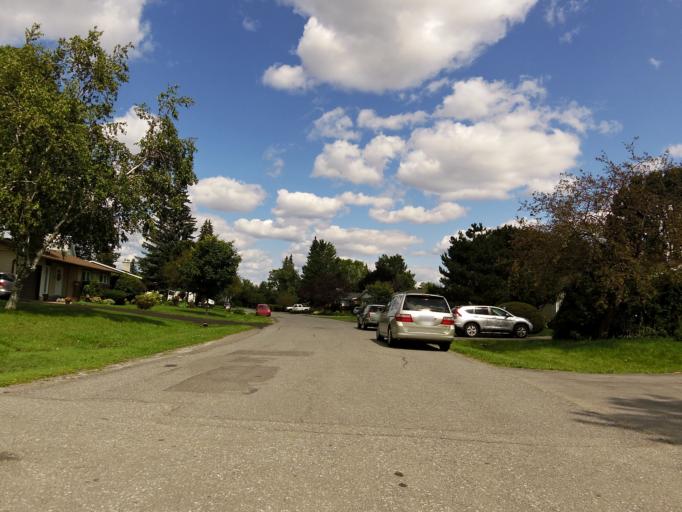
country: CA
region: Ontario
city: Bells Corners
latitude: 45.3467
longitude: -75.8200
